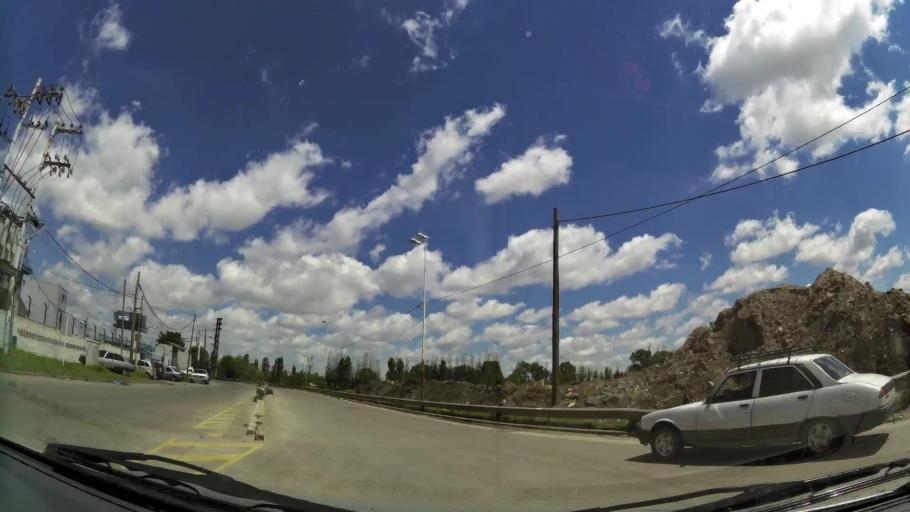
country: AR
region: Buenos Aires F.D.
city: Villa Lugano
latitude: -34.6826
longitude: -58.4404
